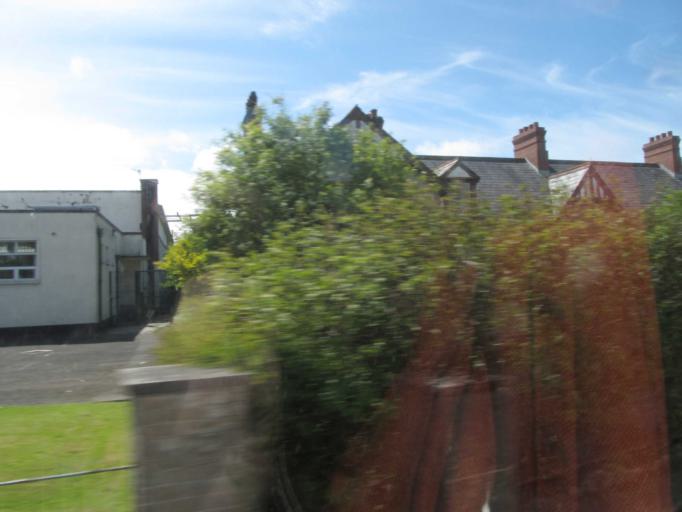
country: GB
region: Northern Ireland
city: Bushmills
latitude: 55.2044
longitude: -6.5259
